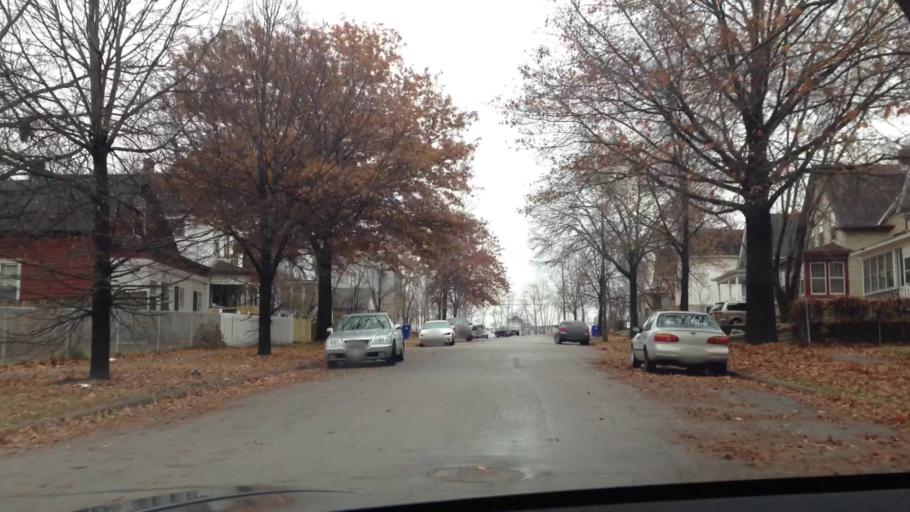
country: US
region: Minnesota
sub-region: Ramsey County
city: Saint Paul
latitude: 44.9678
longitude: -93.0774
